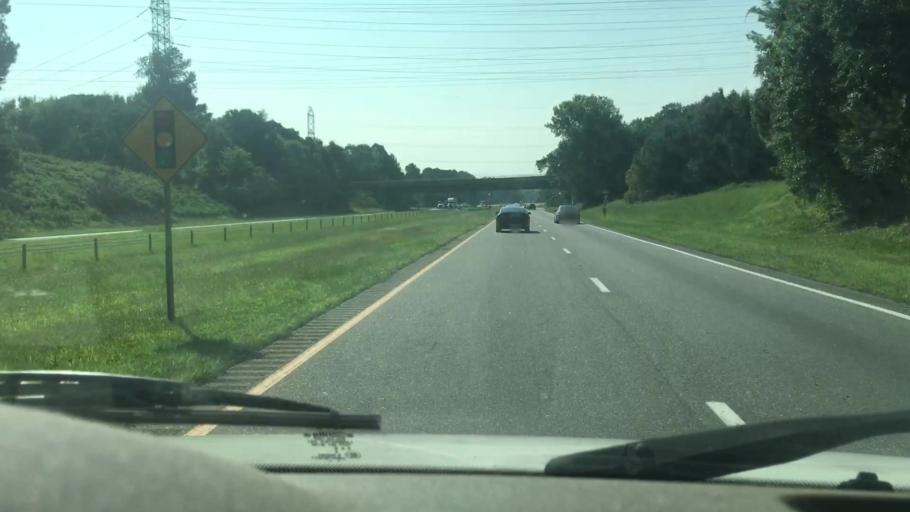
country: US
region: North Carolina
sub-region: Lincoln County
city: Lowesville
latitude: 35.3565
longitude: -80.9801
